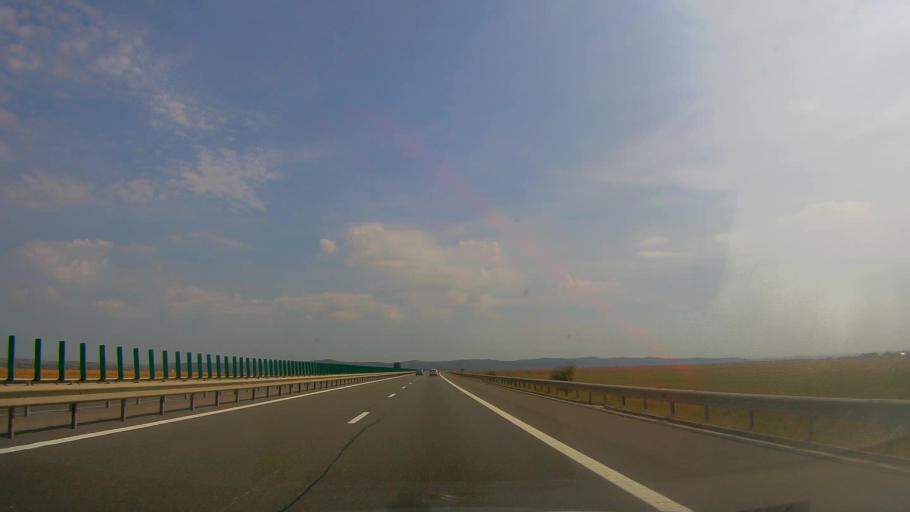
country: RO
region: Cluj
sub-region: Municipiul Campia Turzii
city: Campia Turzii
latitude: 46.5260
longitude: 23.8404
